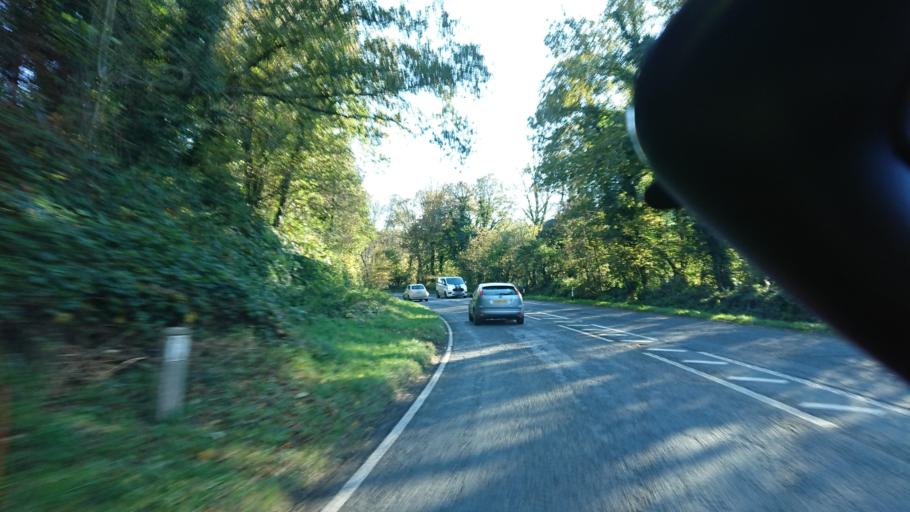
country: GB
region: England
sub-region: Cornwall
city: Pillaton
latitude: 50.3953
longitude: -4.3468
